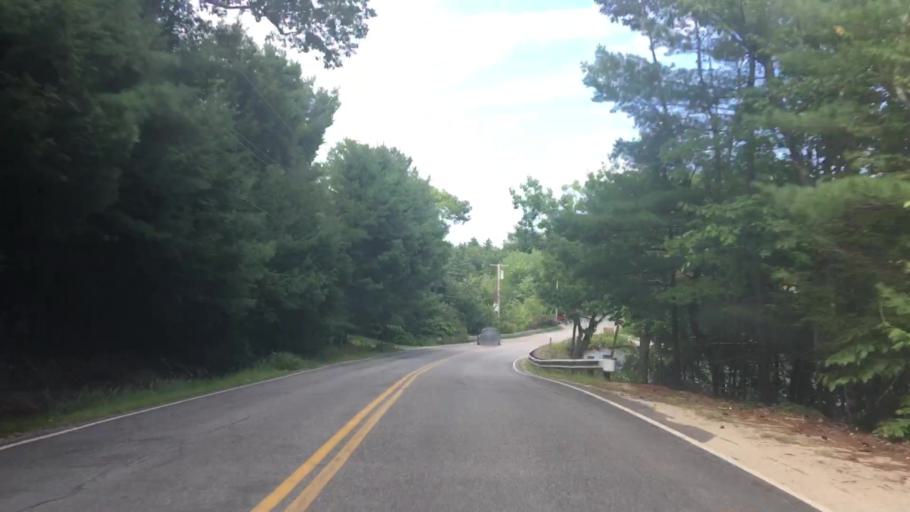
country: US
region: Maine
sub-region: Oxford County
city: Oxford
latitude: 44.1093
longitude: -70.5076
